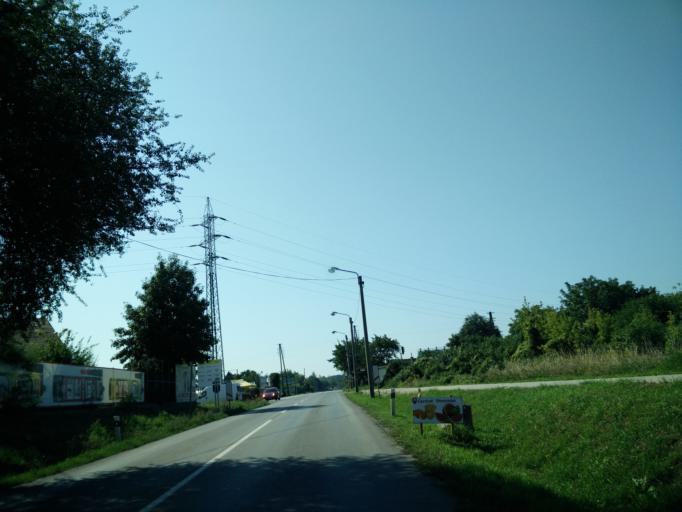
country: SK
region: Nitriansky
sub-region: Okres Nitra
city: Nitra
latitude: 48.3262
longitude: 18.0402
